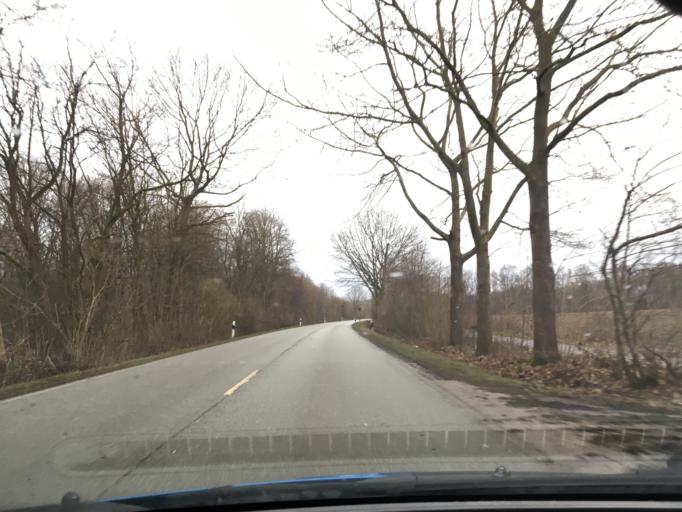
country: DE
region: Schleswig-Holstein
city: Siebeneichen
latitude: 53.4959
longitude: 10.6130
